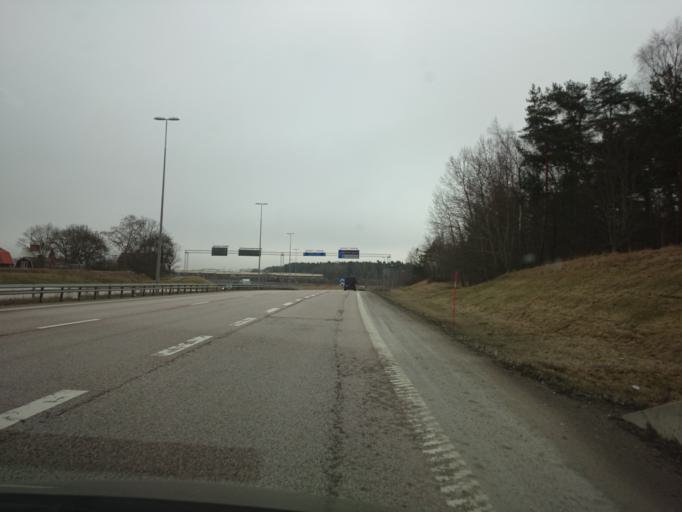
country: SE
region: Uppsala
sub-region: Uppsala Kommun
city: Gamla Uppsala
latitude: 59.8805
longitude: 17.6287
